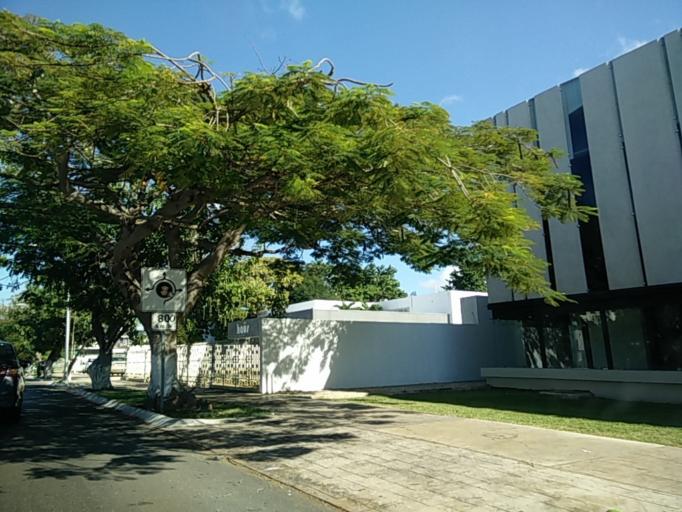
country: MX
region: Yucatan
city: Merida
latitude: 20.9970
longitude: -89.6161
